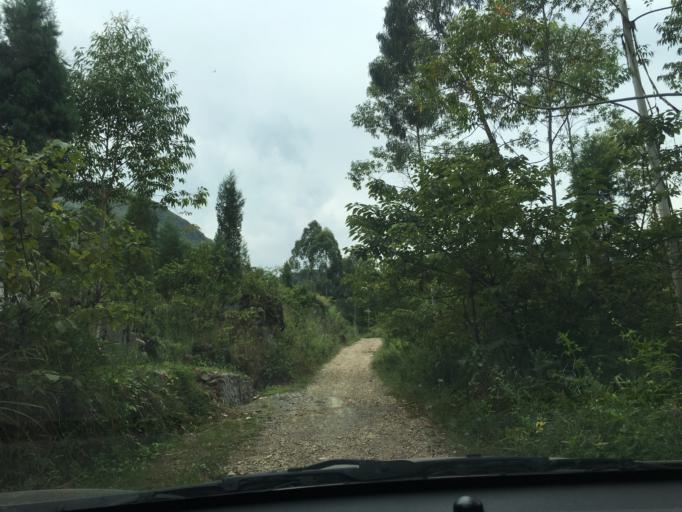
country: CN
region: Guangxi Zhuangzu Zizhiqu
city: Xinzhou
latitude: 25.3798
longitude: 105.6349
